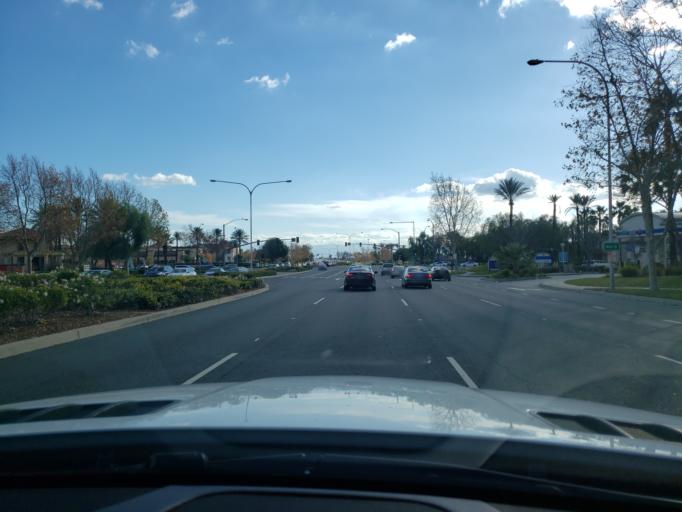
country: US
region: California
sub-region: San Bernardino County
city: Rancho Cucamonga
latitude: 34.0731
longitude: -117.5579
